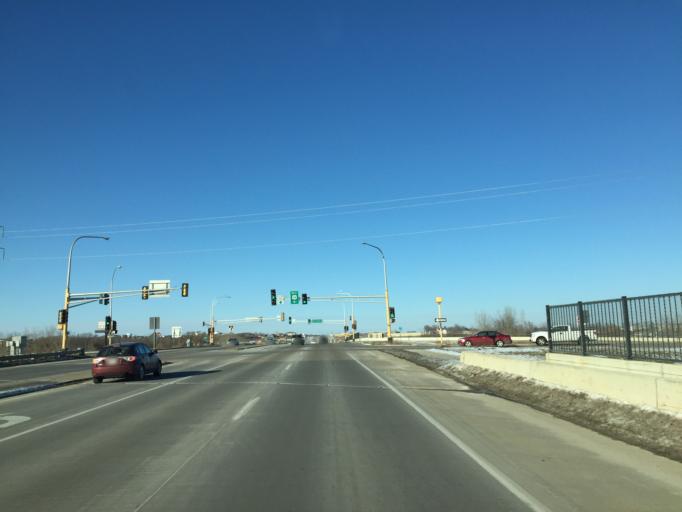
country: US
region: Minnesota
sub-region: Olmsted County
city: Rochester
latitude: 44.0369
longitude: -92.5177
